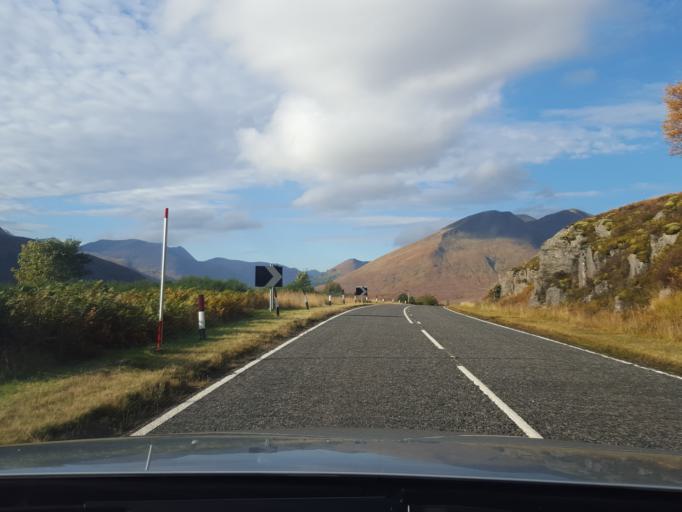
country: GB
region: Scotland
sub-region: Highland
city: Fort William
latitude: 57.1537
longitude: -5.1332
